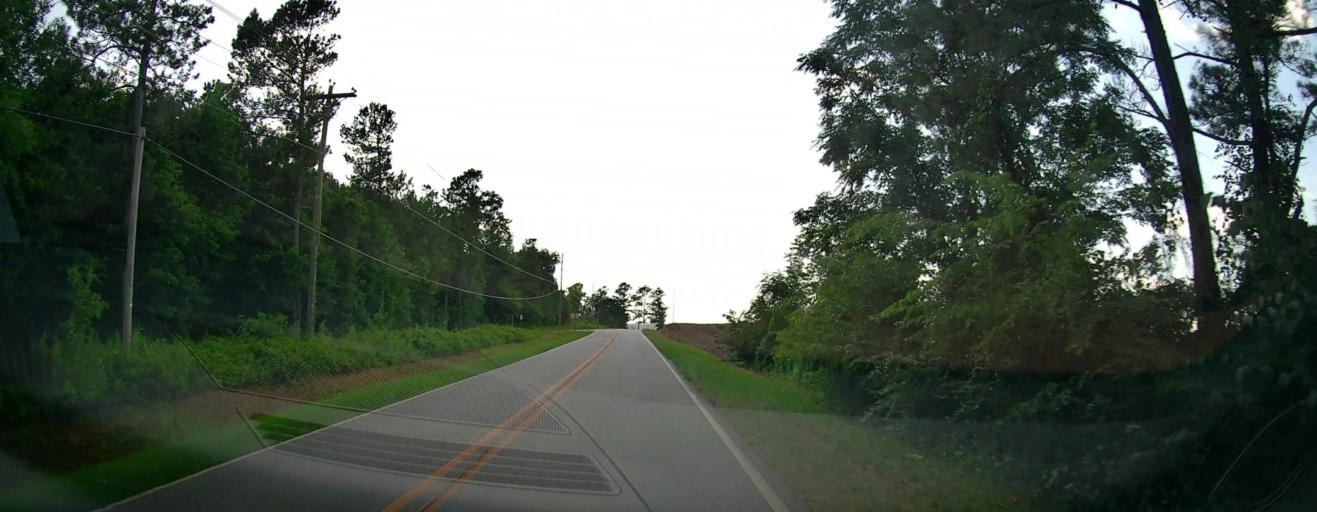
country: US
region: Georgia
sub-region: Henry County
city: Locust Grove
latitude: 33.2235
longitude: -84.1008
